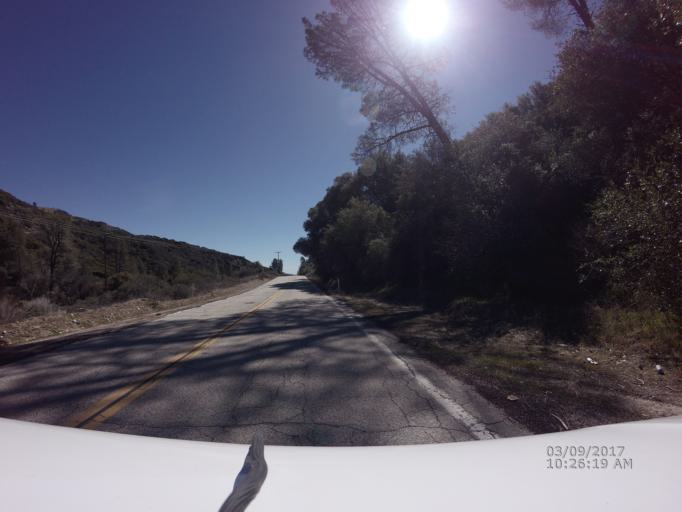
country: US
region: California
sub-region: Los Angeles County
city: Green Valley
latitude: 34.6983
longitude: -118.5063
